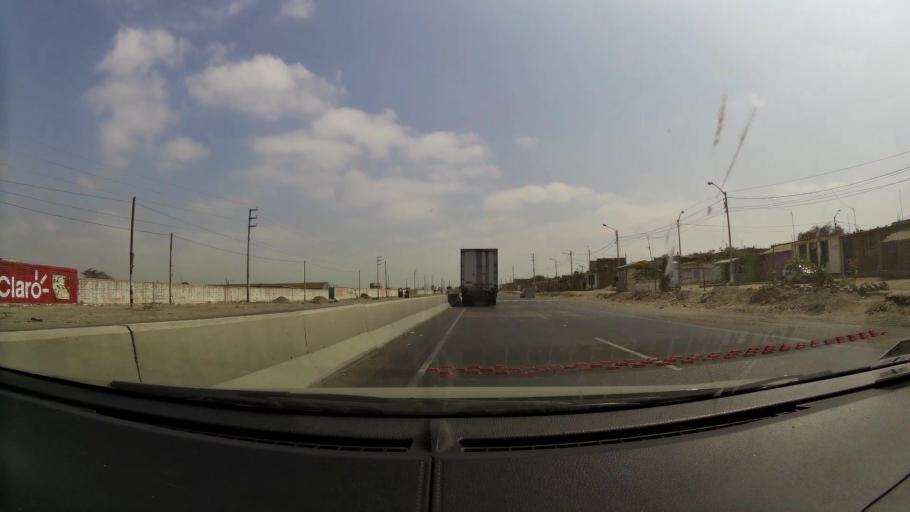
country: PE
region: La Libertad
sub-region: Ascope
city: Chicama
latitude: -7.8695
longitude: -79.1353
